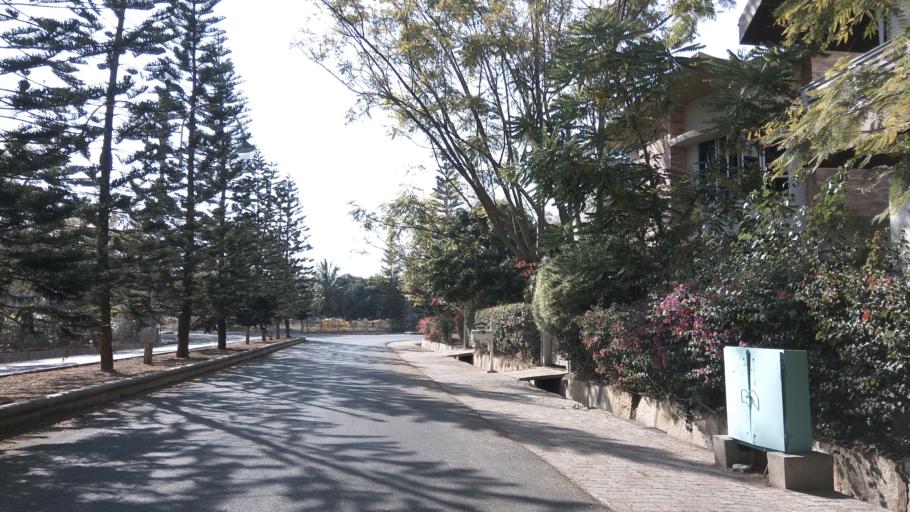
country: IN
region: Karnataka
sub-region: Bangalore Rural
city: Devanhalli
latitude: 13.2066
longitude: 77.6323
